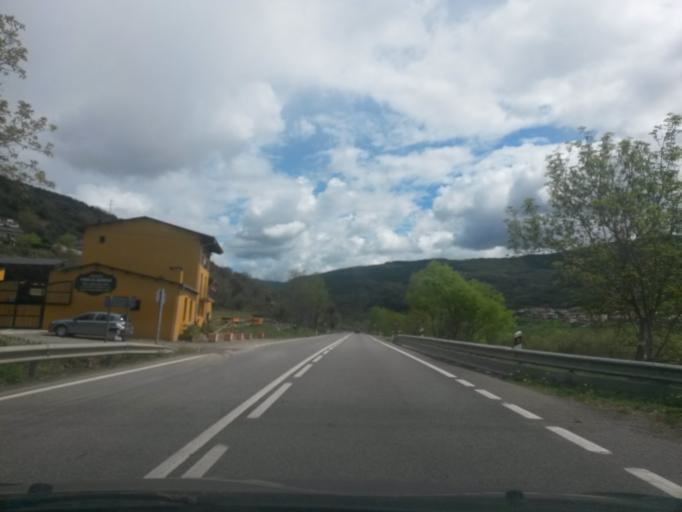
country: ES
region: Catalonia
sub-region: Provincia de Lleida
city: Alas i Cerc
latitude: 42.3590
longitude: 1.4943
